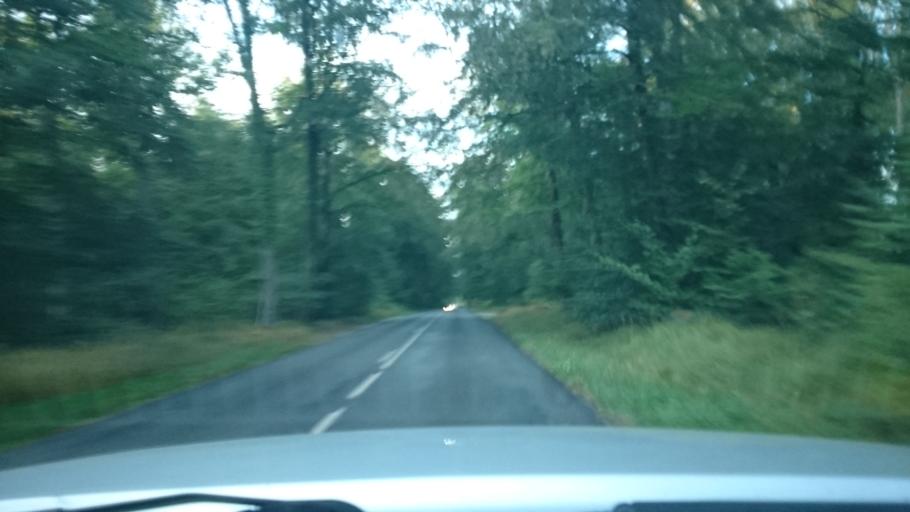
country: FR
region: Ile-de-France
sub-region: Departement de Seine-et-Marne
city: Bois-le-Roi
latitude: 48.4499
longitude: 2.7213
